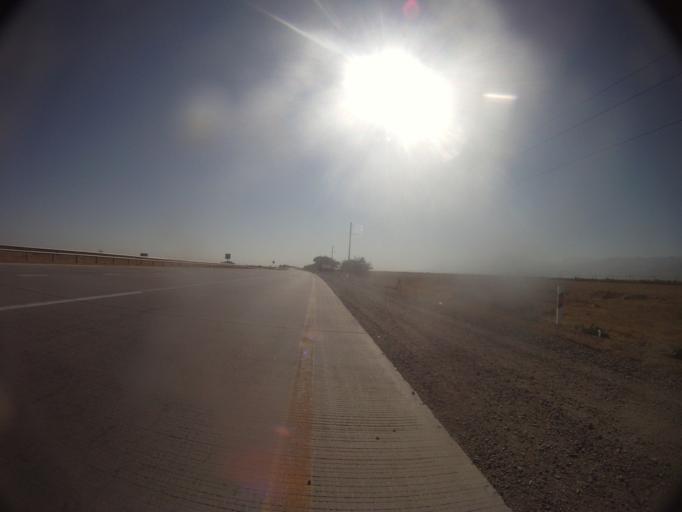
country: KZ
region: Zhambyl
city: Sarykemer
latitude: 43.0082
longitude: 71.8133
